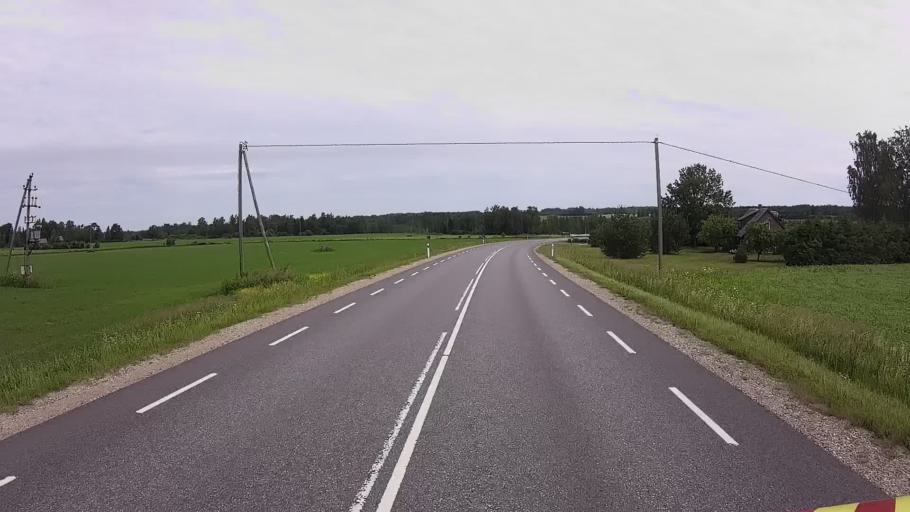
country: EE
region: Viljandimaa
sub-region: Karksi vald
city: Karksi-Nuia
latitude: 58.1419
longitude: 25.5873
